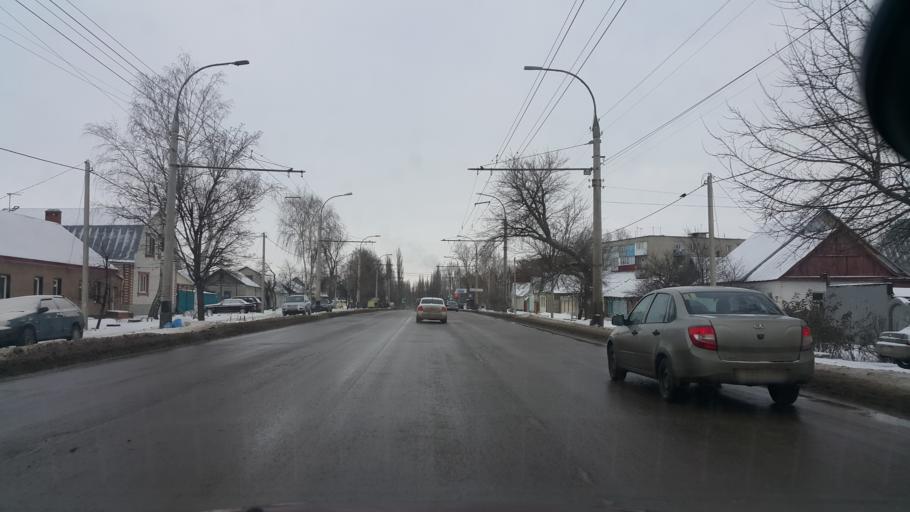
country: RU
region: Tambov
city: Tambov
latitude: 52.7310
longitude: 41.4023
